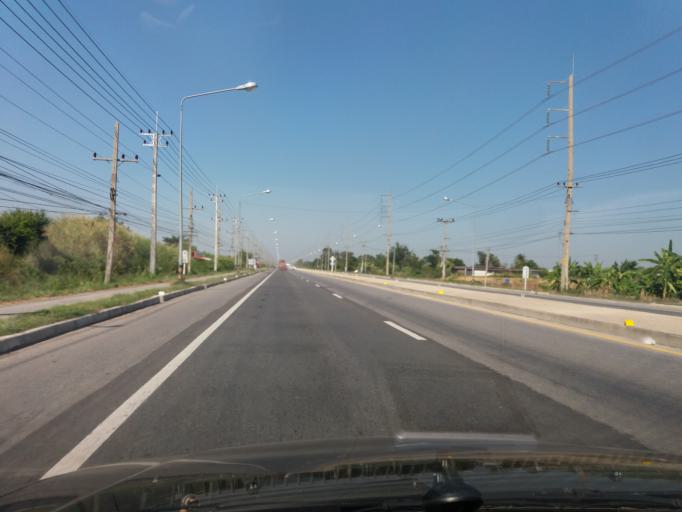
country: TH
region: Chai Nat
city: Manorom
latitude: 15.2820
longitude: 100.0962
